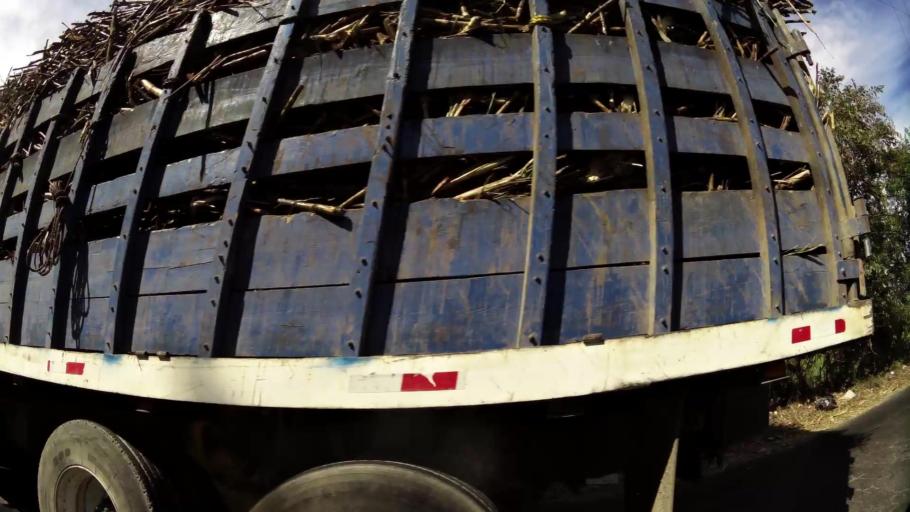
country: SV
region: San Salvador
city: Aguilares
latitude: 13.9610
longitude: -89.1831
